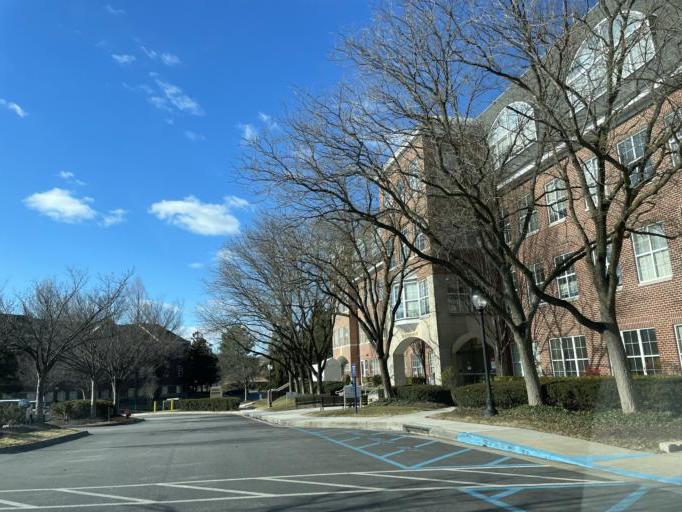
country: US
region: Maryland
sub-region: Baltimore County
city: Mays Chapel
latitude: 39.4207
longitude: -76.6662
